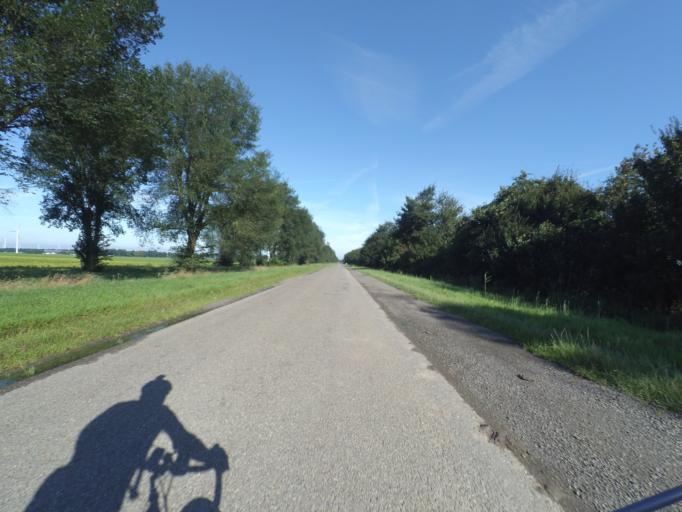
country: NL
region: Flevoland
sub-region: Gemeente Zeewolde
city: Zeewolde
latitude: 52.3781
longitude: 5.5072
